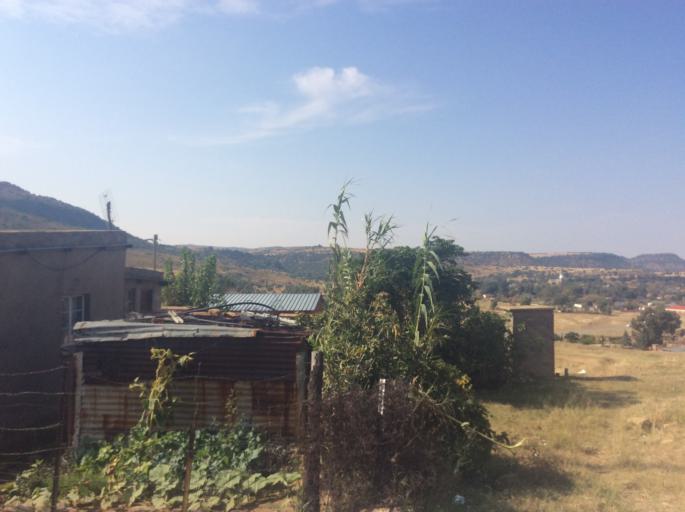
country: LS
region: Mafeteng
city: Mafeteng
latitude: -29.7214
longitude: 27.0339
